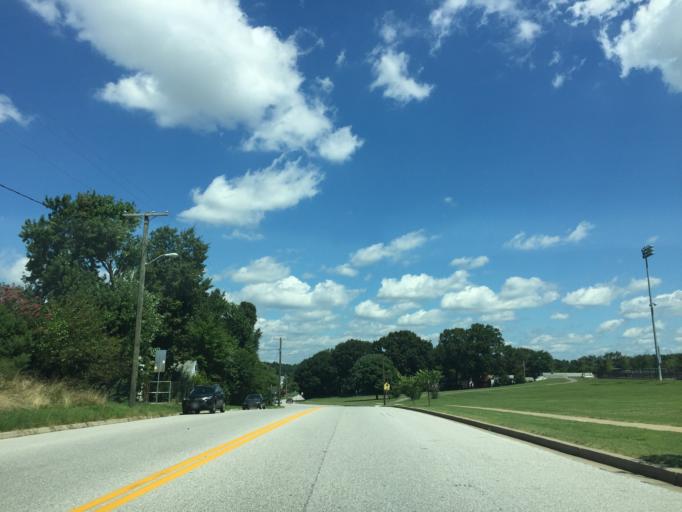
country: US
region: Maryland
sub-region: Baltimore County
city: Dundalk
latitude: 39.2681
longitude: -76.5173
